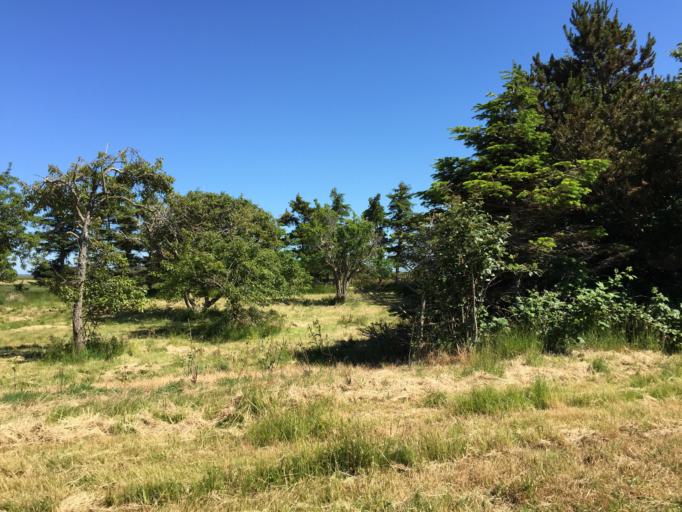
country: DE
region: Schleswig-Holstein
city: List
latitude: 55.1717
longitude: 8.5527
